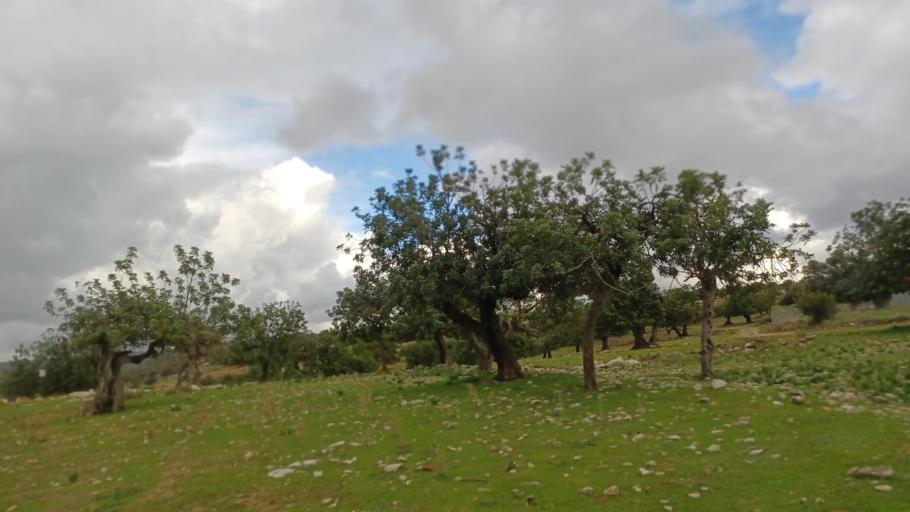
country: CY
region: Limassol
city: Sotira
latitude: 34.7253
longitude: 32.8250
